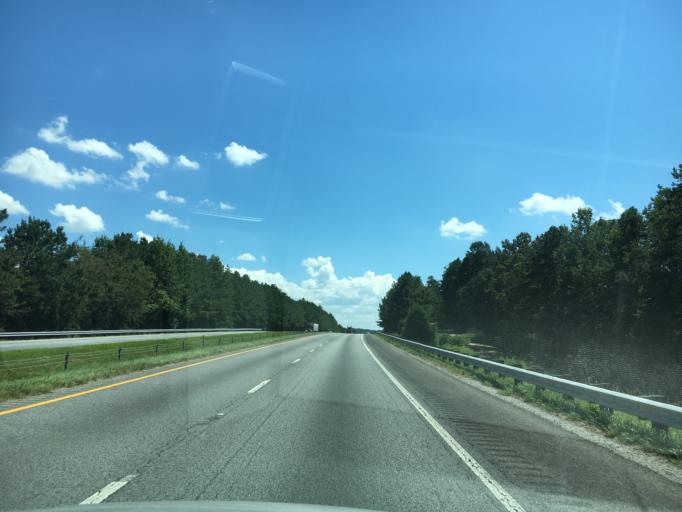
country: US
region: South Carolina
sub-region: Spartanburg County
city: Woodruff
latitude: 34.7767
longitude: -81.9538
